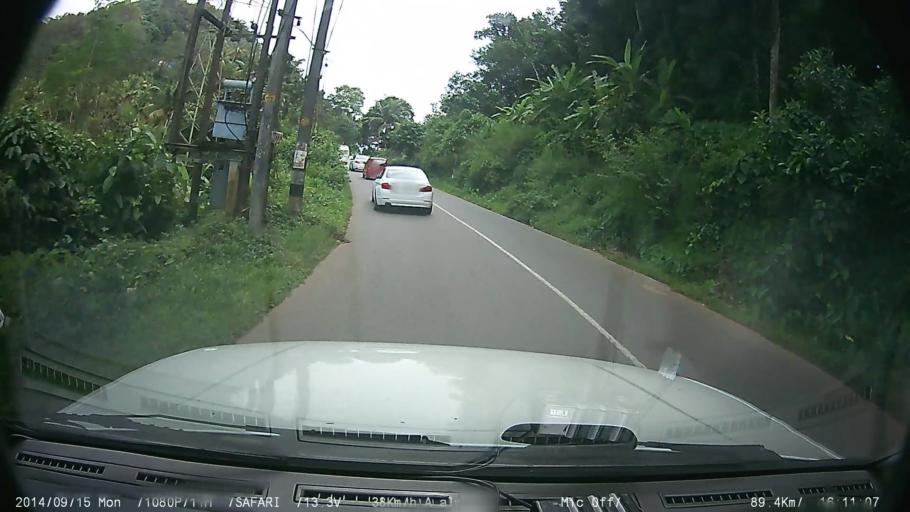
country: IN
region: Kerala
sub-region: Ernakulam
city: Muvattupuzha
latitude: 9.9277
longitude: 76.5792
